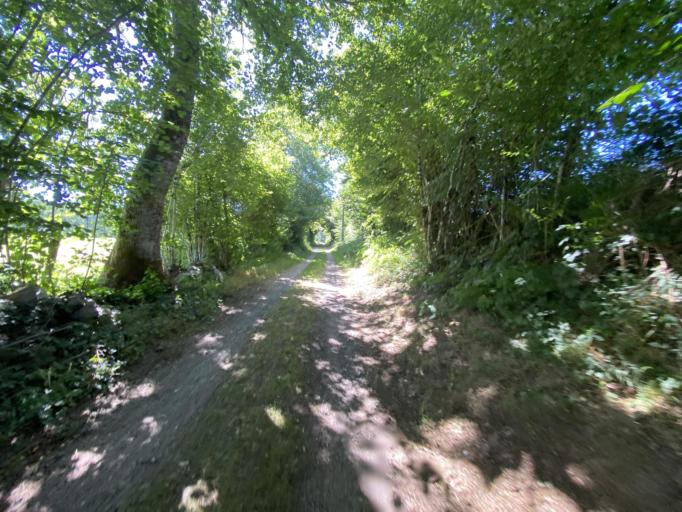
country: FR
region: Bourgogne
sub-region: Departement de la Cote-d'Or
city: Saulieu
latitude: 47.2951
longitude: 4.1239
